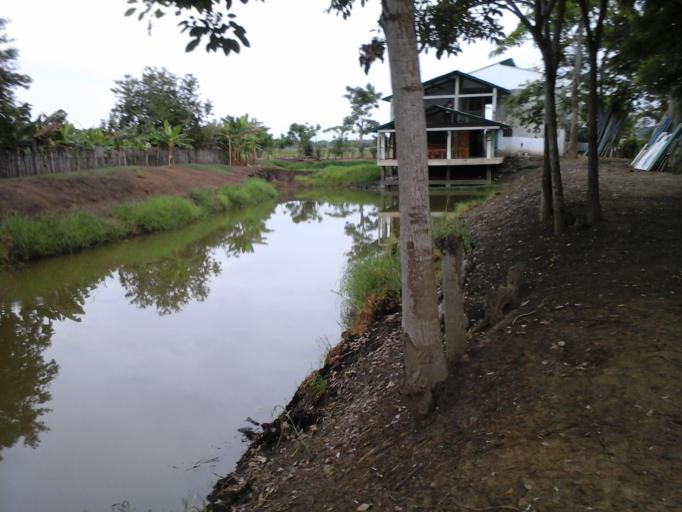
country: CO
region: Cordoba
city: Lorica
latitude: 9.1341
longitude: -75.8409
